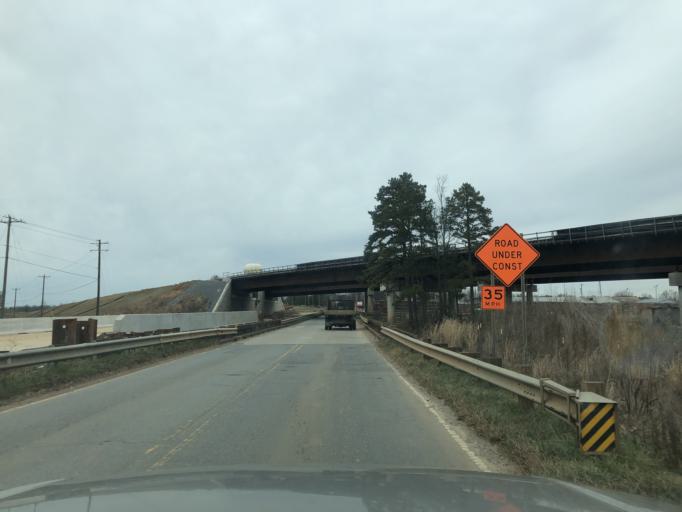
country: US
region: North Carolina
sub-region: Cleveland County
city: Shelby
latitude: 35.3157
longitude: -81.4942
